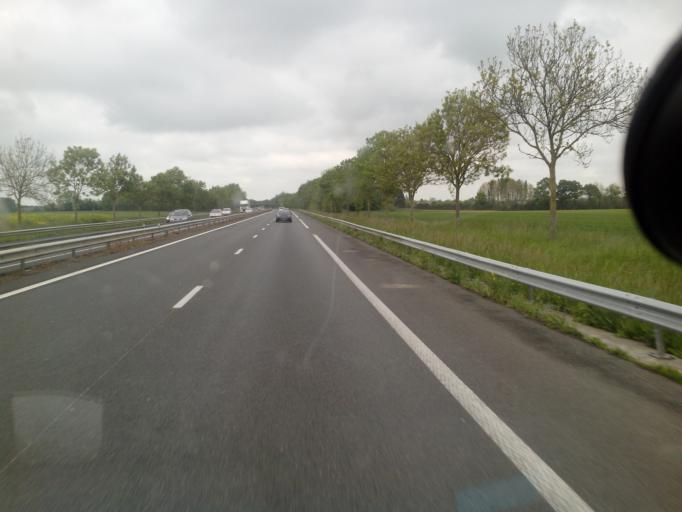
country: FR
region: Lower Normandy
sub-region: Departement du Calvados
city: Grainville-sur-Odon
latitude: 49.1386
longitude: -0.5488
